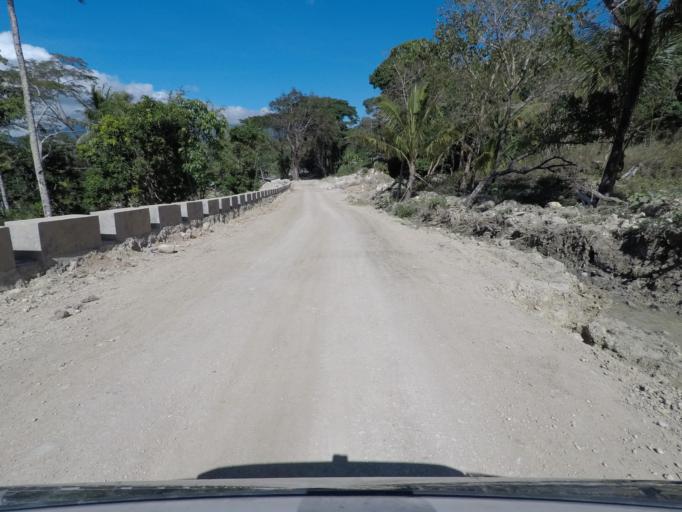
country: TL
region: Baucau
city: Venilale
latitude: -8.6469
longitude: 126.3734
